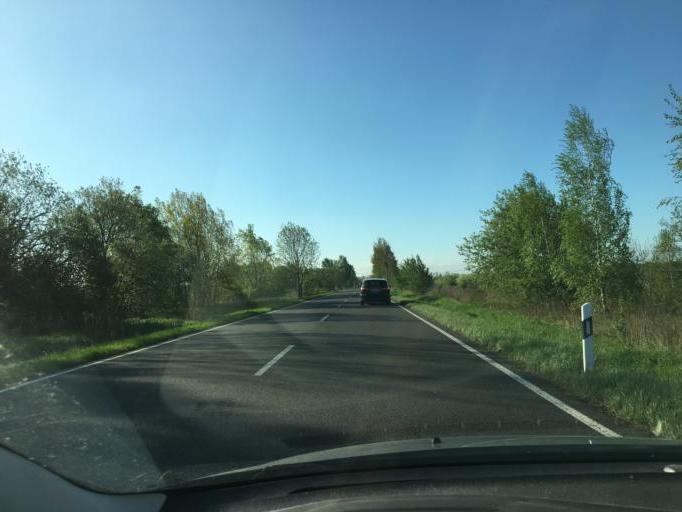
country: DE
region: Saxony
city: Espenhain
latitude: 51.2100
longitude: 12.4507
